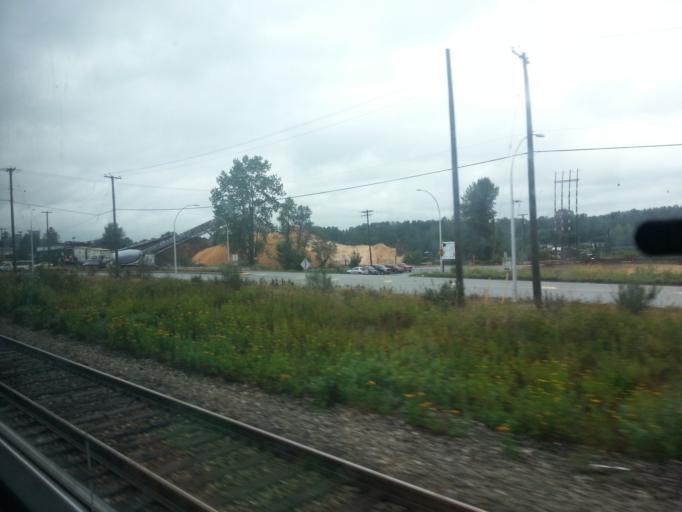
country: CA
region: British Columbia
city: Pitt Meadows
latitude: 49.1814
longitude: -122.6888
